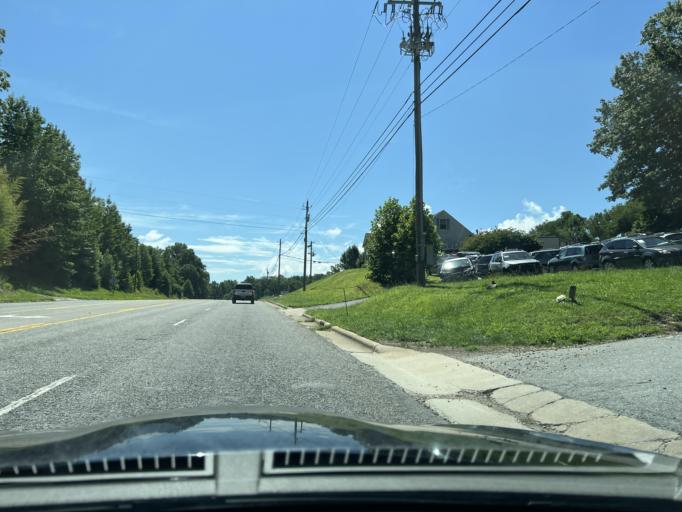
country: US
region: North Carolina
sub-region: Buncombe County
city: Fairview
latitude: 35.5246
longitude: -82.4230
